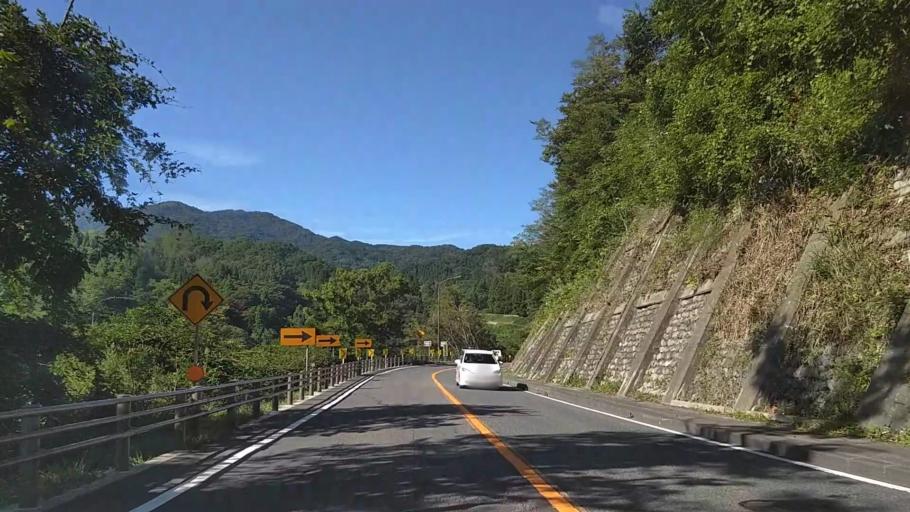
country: JP
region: Nagano
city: Nagano-shi
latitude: 36.6193
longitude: 138.1043
